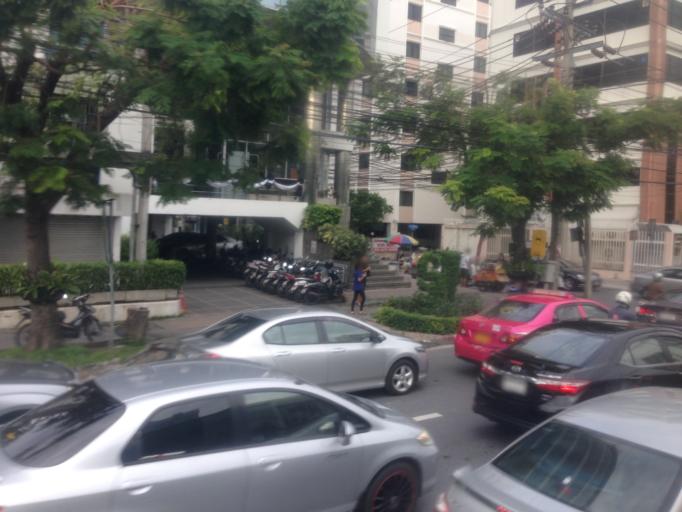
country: TH
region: Bangkok
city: Sathon
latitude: 13.7148
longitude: 100.5336
